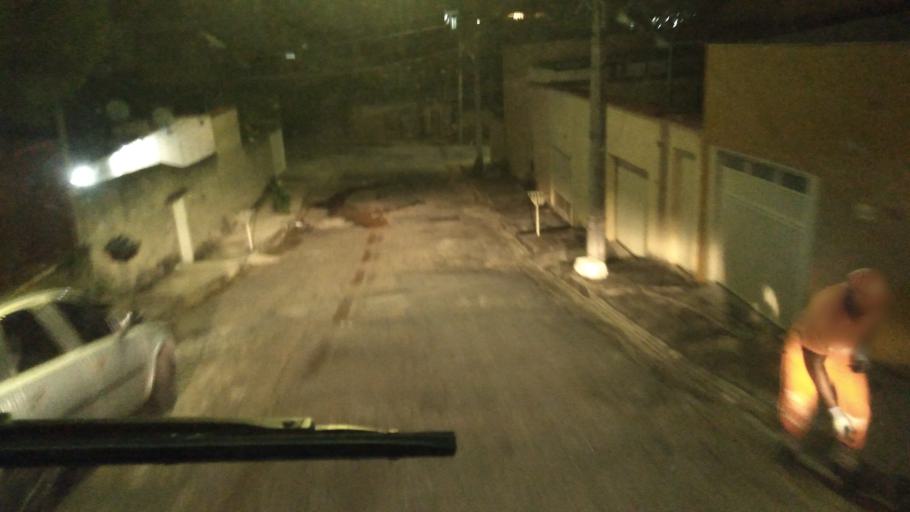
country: BR
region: Minas Gerais
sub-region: Belo Horizonte
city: Belo Horizonte
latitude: -19.8755
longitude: -43.9381
